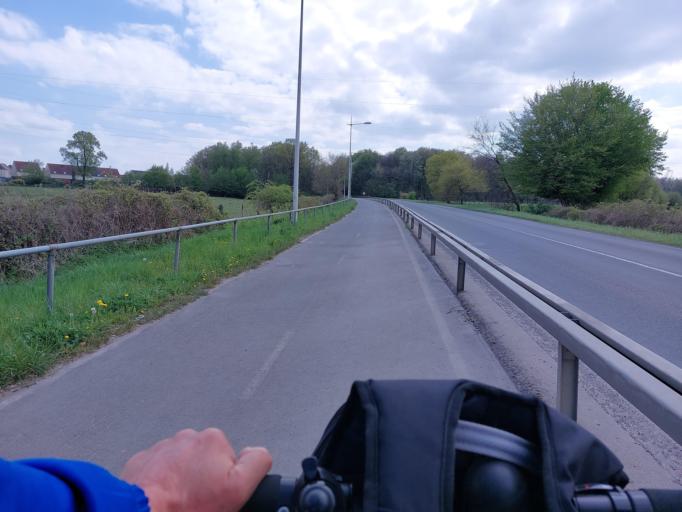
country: FR
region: Nord-Pas-de-Calais
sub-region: Departement du Nord
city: Hautmont
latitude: 50.2597
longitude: 3.8964
